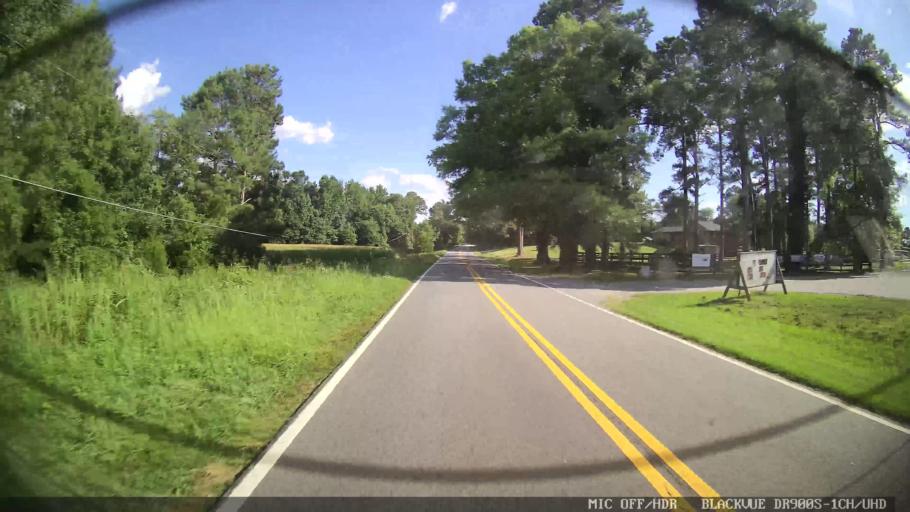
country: US
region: Georgia
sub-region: Bartow County
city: Euharlee
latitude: 34.1624
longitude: -84.9861
